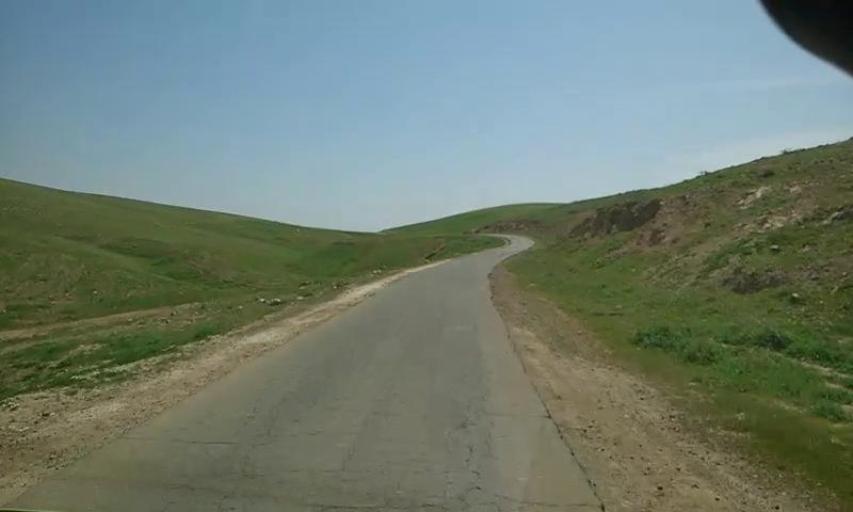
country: PS
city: `Arab ar Rashaydah
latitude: 31.5531
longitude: 35.2504
